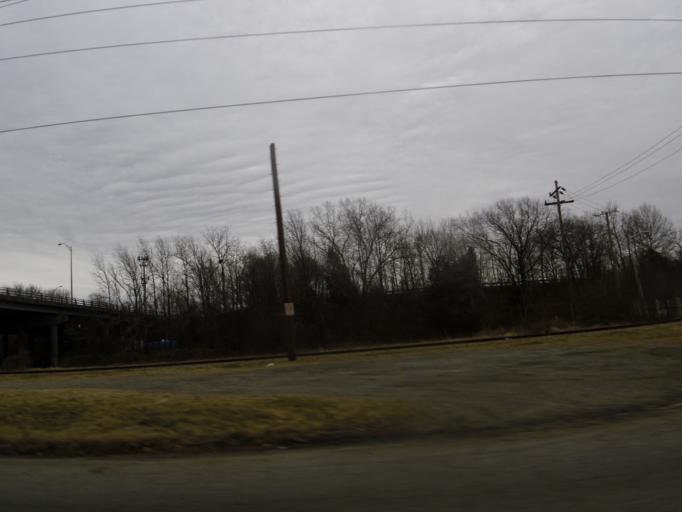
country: US
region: Virginia
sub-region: City of Portsmouth
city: Portsmouth
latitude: 36.8373
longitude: -76.3307
